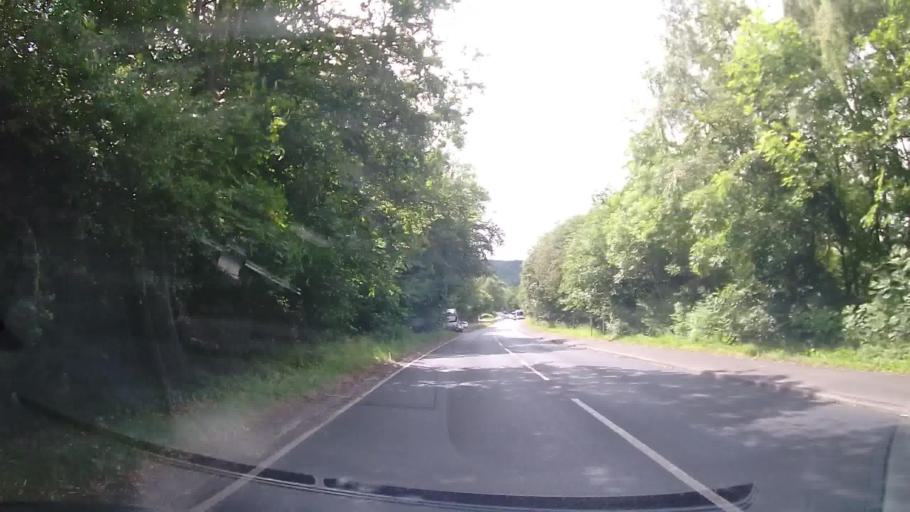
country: GB
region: Wales
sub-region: Denbighshire
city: Bryneglwys
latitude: 52.9784
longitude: -3.3199
